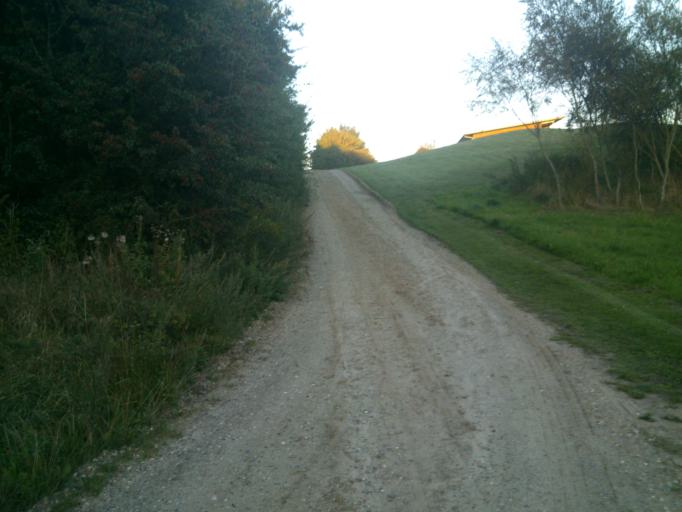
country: DK
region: South Denmark
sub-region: Fredericia Kommune
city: Fredericia
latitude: 55.5715
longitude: 9.7060
